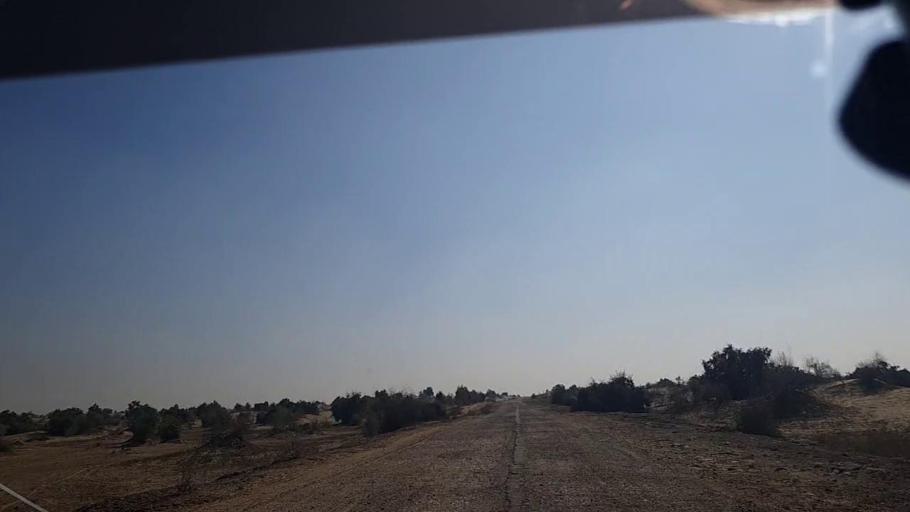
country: PK
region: Sindh
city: Khanpur
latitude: 27.5775
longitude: 69.3054
